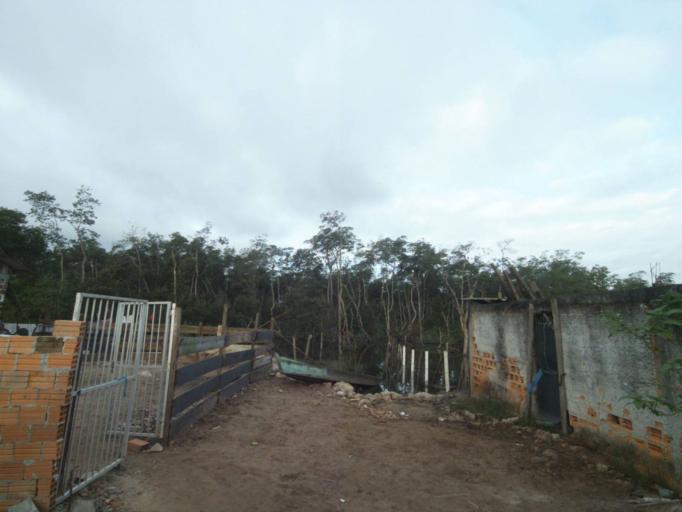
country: BR
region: Parana
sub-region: Paranagua
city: Paranagua
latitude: -25.5368
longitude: -48.5467
